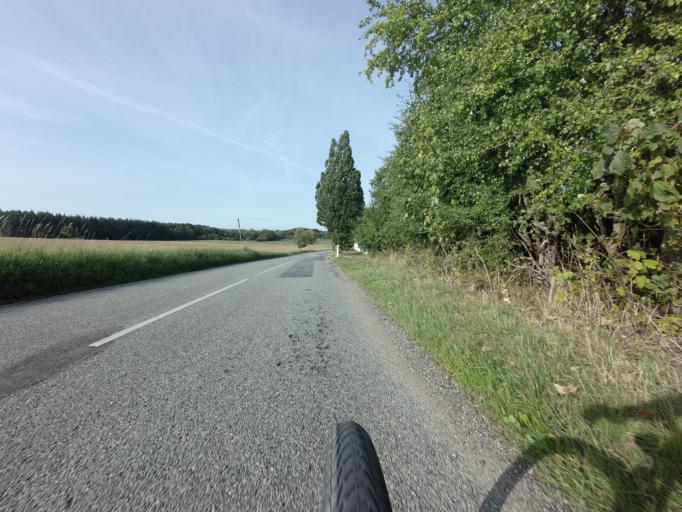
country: DK
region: Zealand
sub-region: Faxe Kommune
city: Fakse Ladeplads
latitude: 55.2003
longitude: 12.1325
